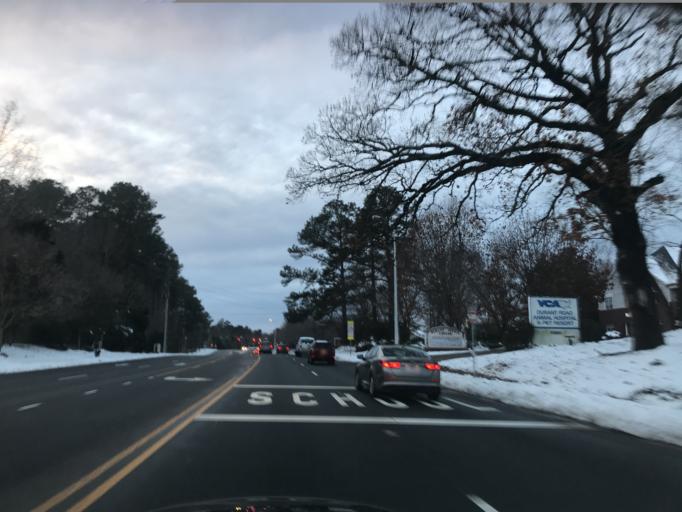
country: US
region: North Carolina
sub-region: Wake County
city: Wake Forest
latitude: 35.9037
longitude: -78.5848
